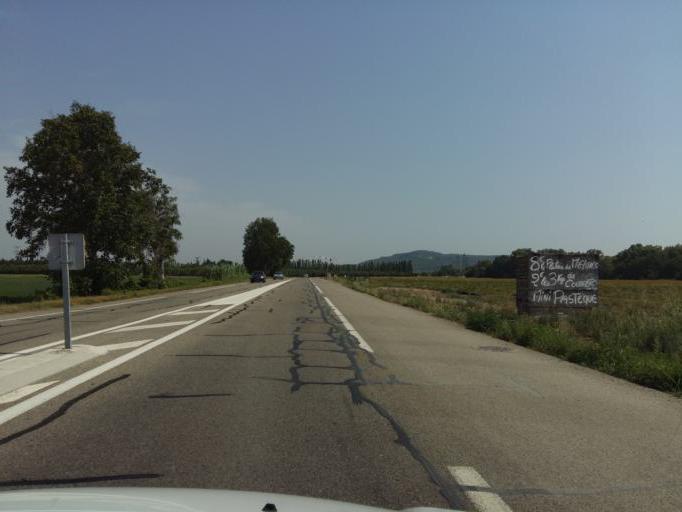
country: FR
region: Provence-Alpes-Cote d'Azur
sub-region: Departement du Vaucluse
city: Bollene
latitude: 44.2802
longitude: 4.7206
